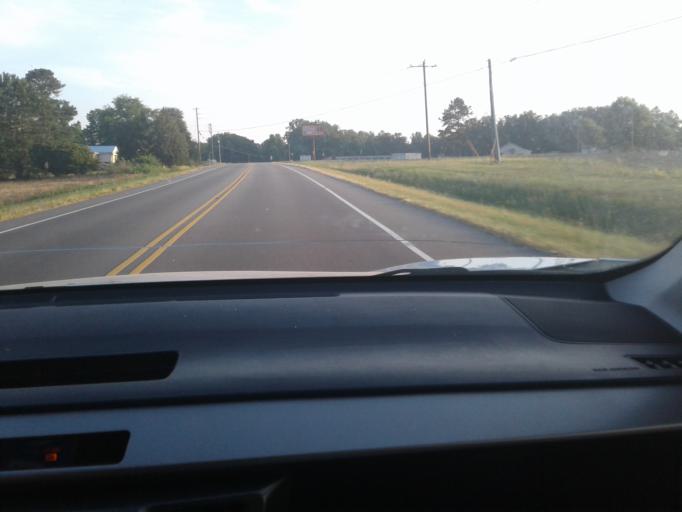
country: US
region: North Carolina
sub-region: Harnett County
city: Lillington
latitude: 35.4556
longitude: -78.8295
